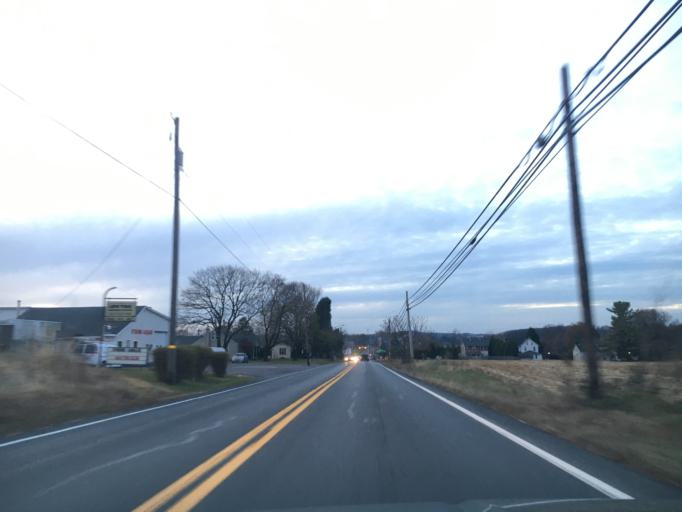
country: US
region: Pennsylvania
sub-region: Lehigh County
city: Egypt
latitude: 40.6522
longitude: -75.5425
